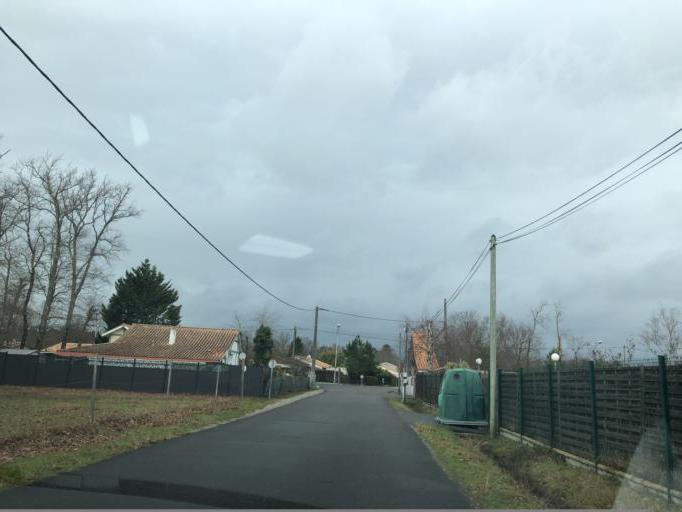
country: FR
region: Aquitaine
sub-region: Departement de la Gironde
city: Hourtin
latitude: 45.1815
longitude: -1.0758
